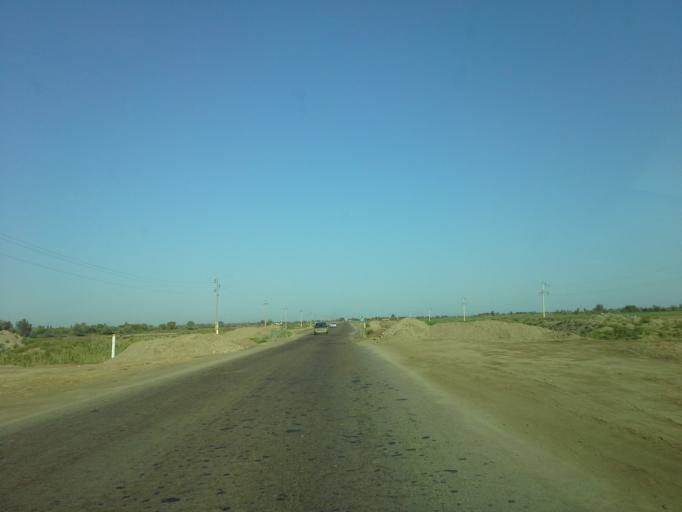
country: UZ
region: Karakalpakstan
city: Khujayli
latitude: 42.2225
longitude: 59.4850
